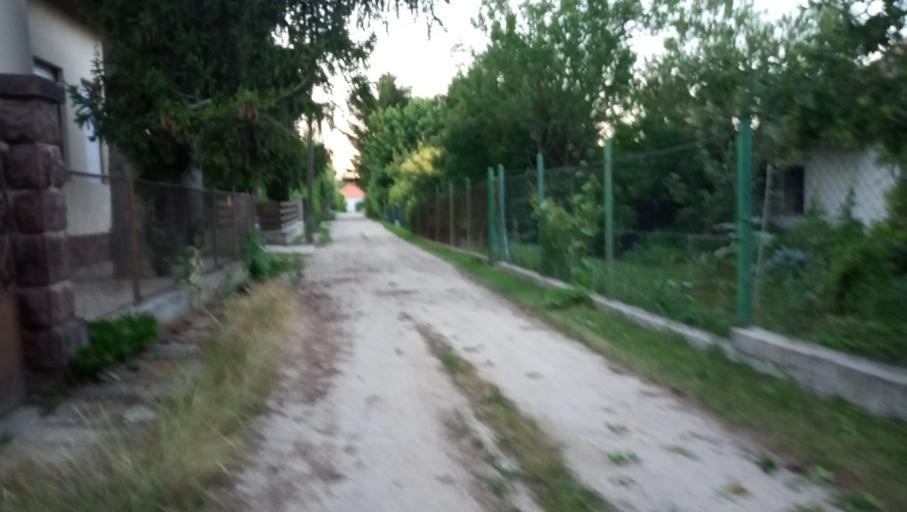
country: HU
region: Veszprem
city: Balatonkenese
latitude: 47.0352
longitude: 18.1022
